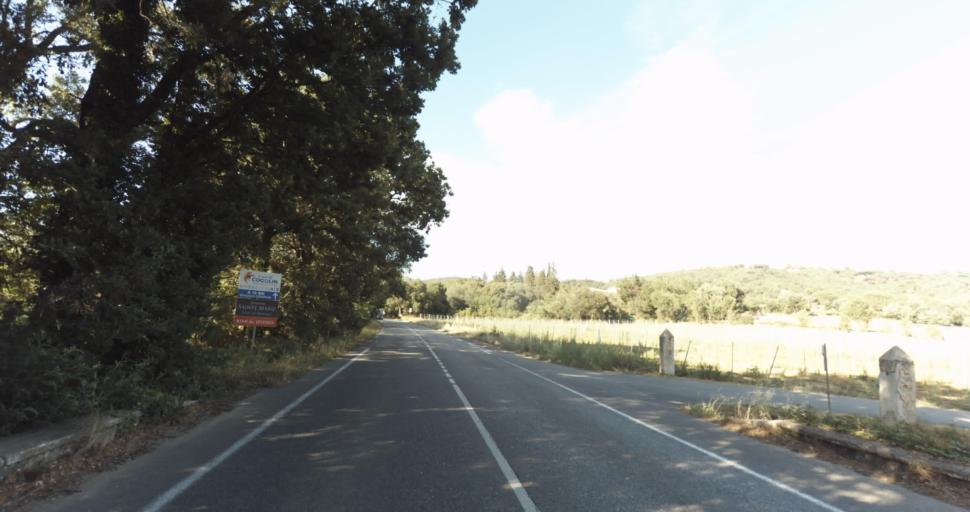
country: FR
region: Provence-Alpes-Cote d'Azur
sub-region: Departement du Var
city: Gassin
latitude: 43.2252
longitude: 6.5713
